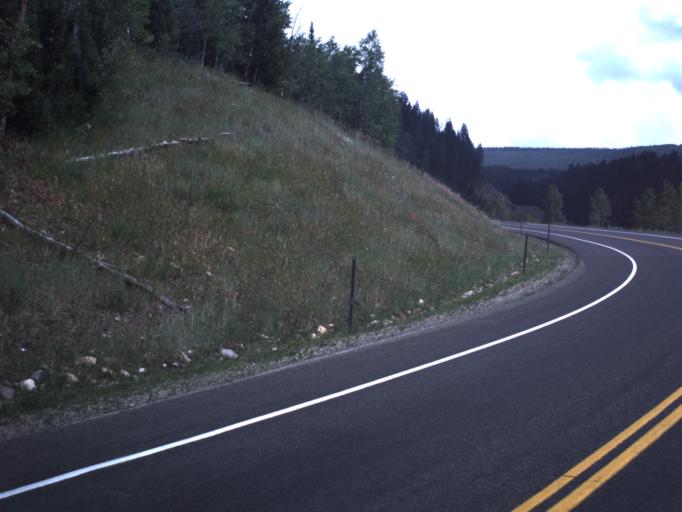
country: US
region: Utah
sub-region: Summit County
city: Francis
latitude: 40.5142
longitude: -111.0636
